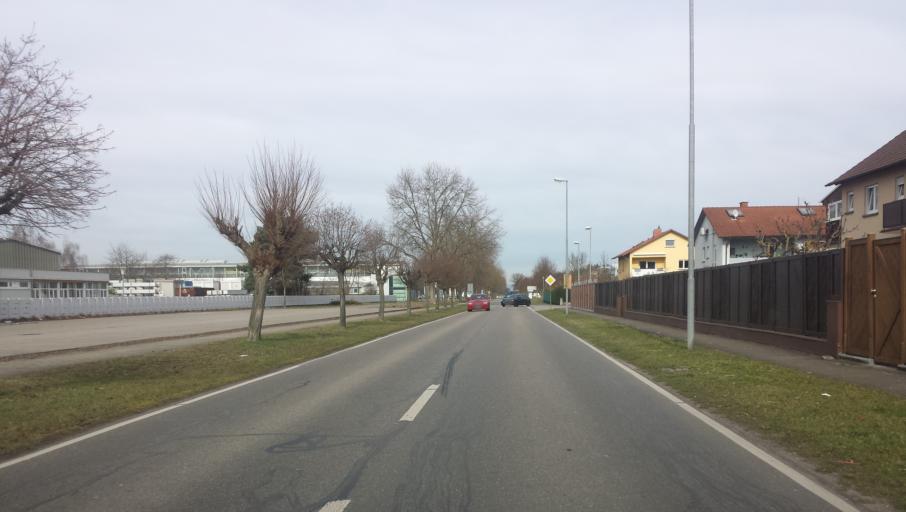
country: DE
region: Baden-Wuerttemberg
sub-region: Karlsruhe Region
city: Waghausel
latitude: 49.2483
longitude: 8.5432
